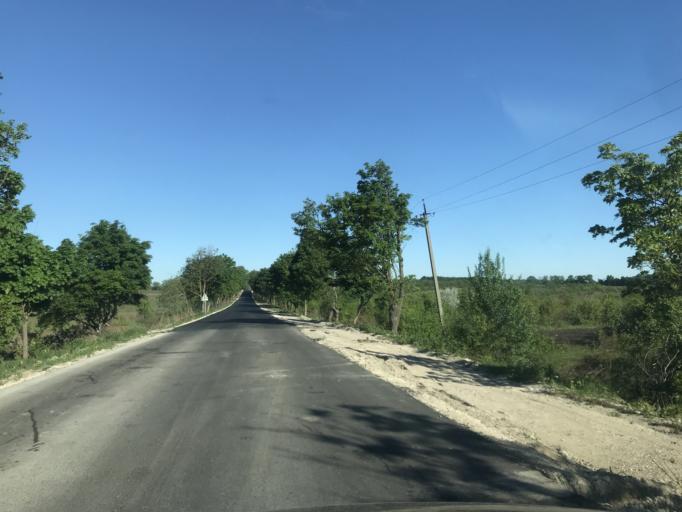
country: MD
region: Chisinau
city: Cricova
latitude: 47.2540
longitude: 28.8072
